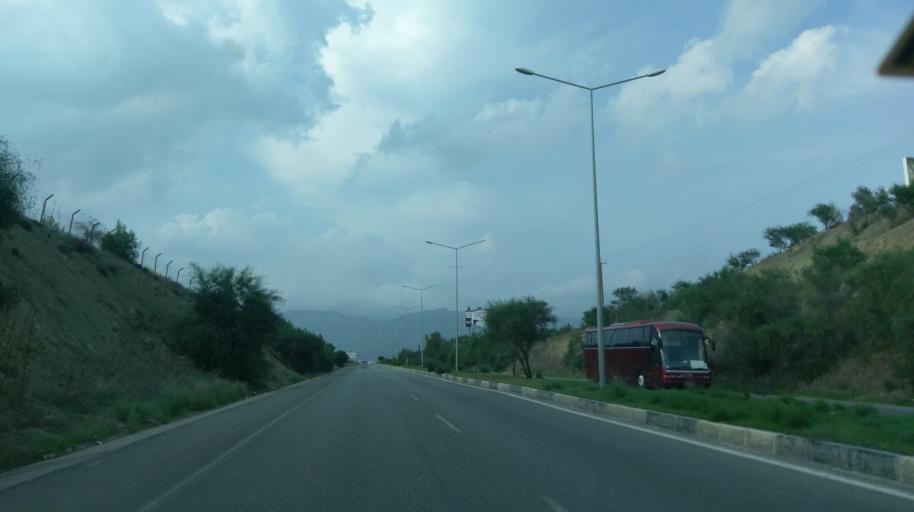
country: CY
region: Keryneia
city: Kyrenia
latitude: 35.2488
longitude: 33.3048
